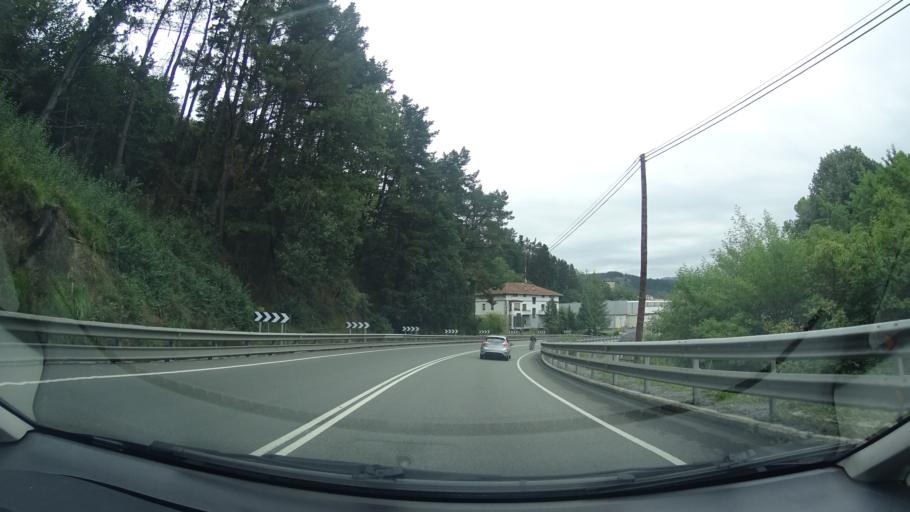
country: ES
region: Basque Country
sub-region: Bizkaia
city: Galdakao
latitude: 43.2222
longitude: -2.8174
